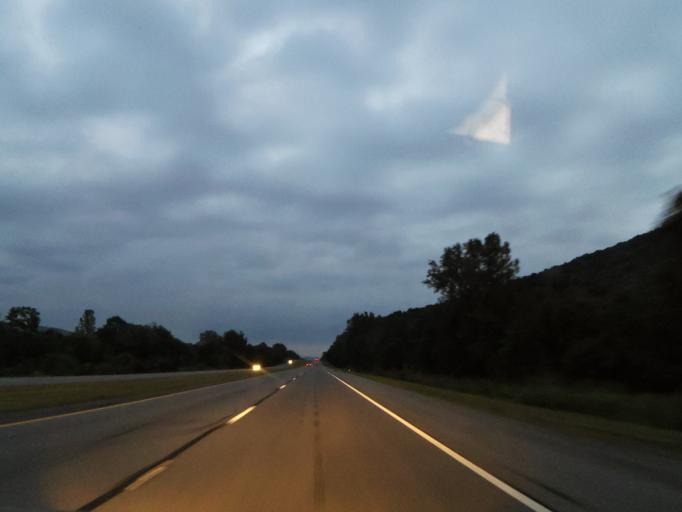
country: US
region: Alabama
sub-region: Madison County
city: New Hope
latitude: 34.6505
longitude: -86.3254
